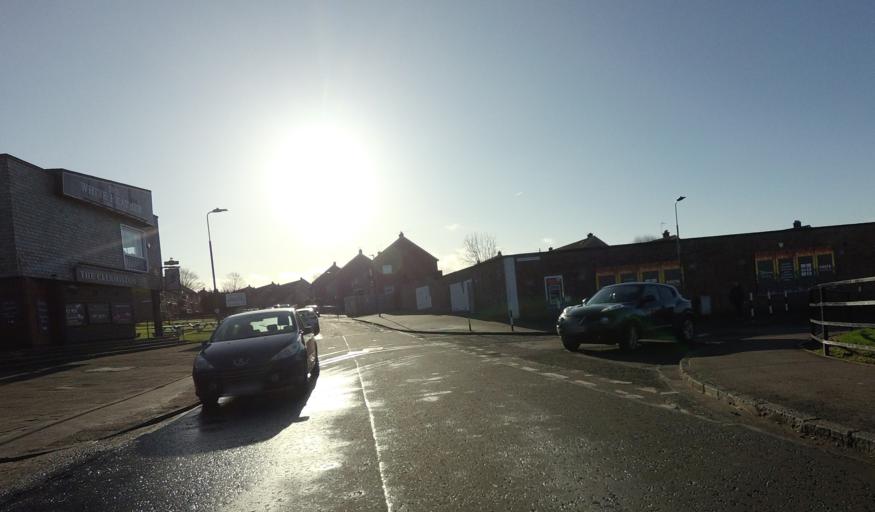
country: GB
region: Scotland
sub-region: Edinburgh
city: Colinton
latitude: 55.9552
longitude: -3.2858
